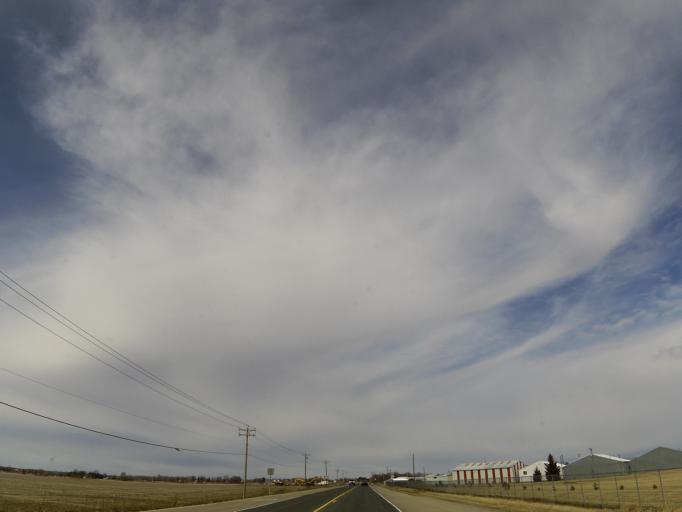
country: US
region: Minnesota
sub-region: Washington County
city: Lake Elmo
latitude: 44.9929
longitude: -92.8626
